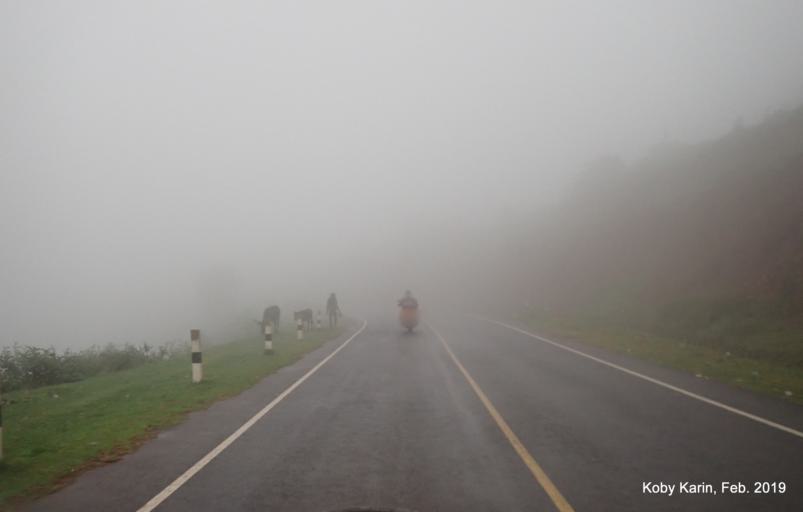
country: UG
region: Western Region
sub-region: Kisoro District
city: Kisoro
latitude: -1.2246
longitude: 29.8023
